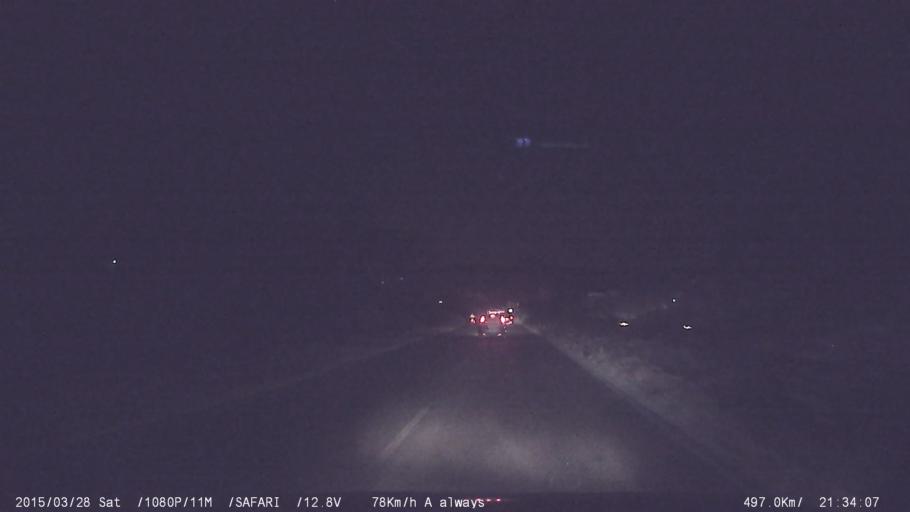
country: IN
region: Karnataka
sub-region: Bangalore Urban
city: Bangalore
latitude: 12.8651
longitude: 77.4355
